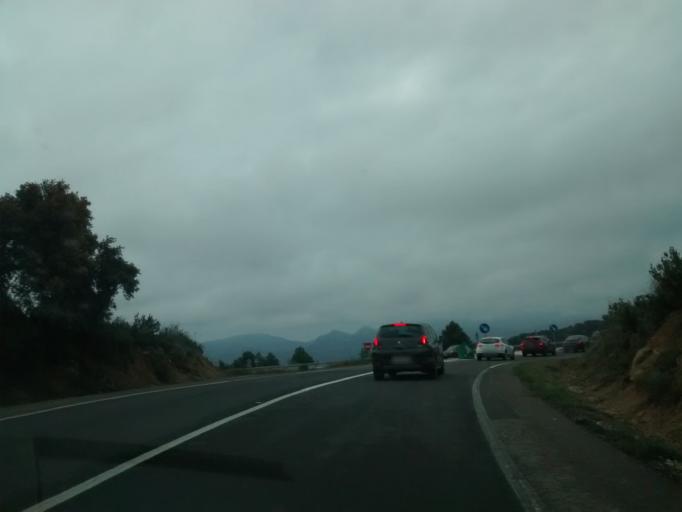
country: ES
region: Catalonia
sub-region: Provincia de Tarragona
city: Bot
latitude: 41.0508
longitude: 0.3656
